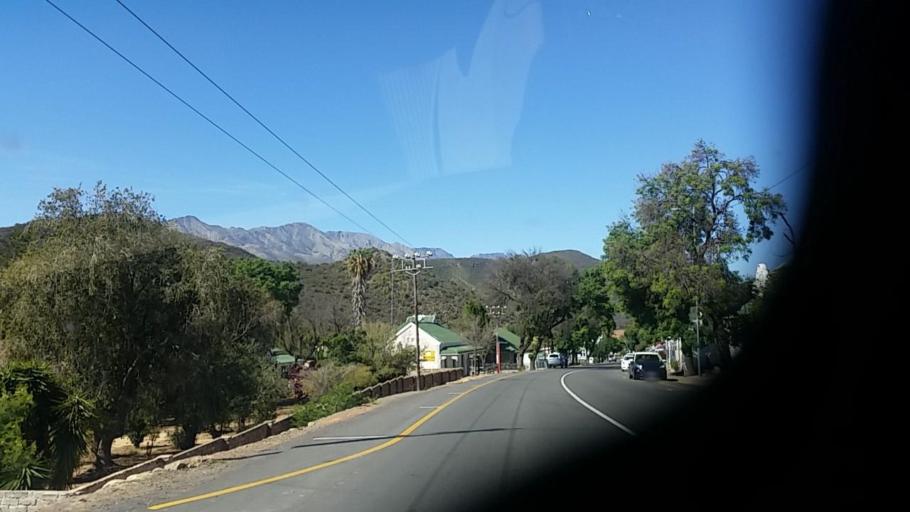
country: ZA
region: Western Cape
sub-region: Eden District Municipality
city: Oudtshoorn
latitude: -33.4895
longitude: 22.5334
